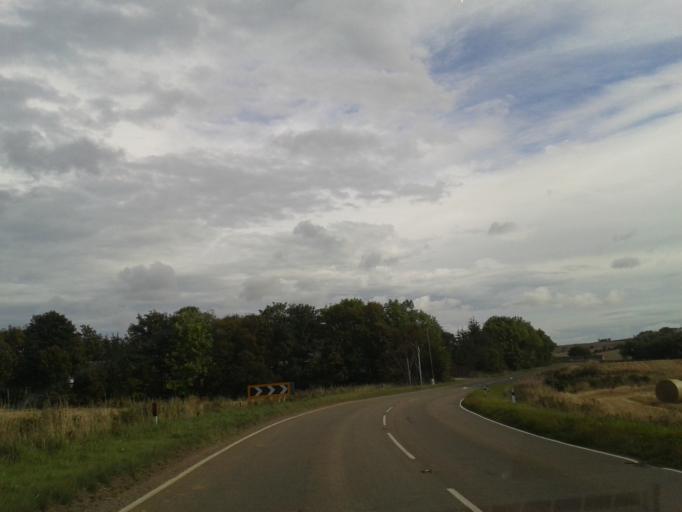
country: GB
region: Scotland
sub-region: Aberdeenshire
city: Whitehills
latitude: 57.6537
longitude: -2.6248
